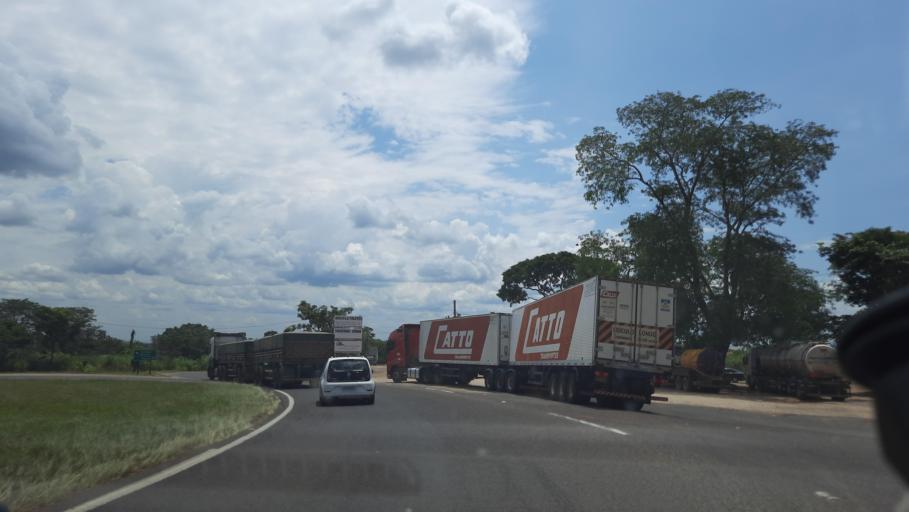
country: BR
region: Sao Paulo
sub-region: Mococa
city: Mococa
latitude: -21.5166
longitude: -47.0322
